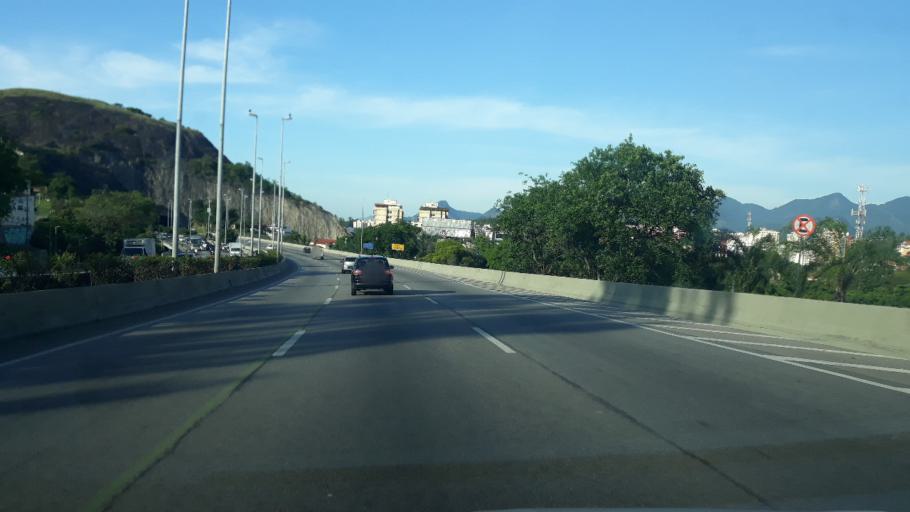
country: BR
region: Rio de Janeiro
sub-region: Sao Joao De Meriti
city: Sao Joao de Meriti
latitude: -22.9262
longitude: -43.3406
